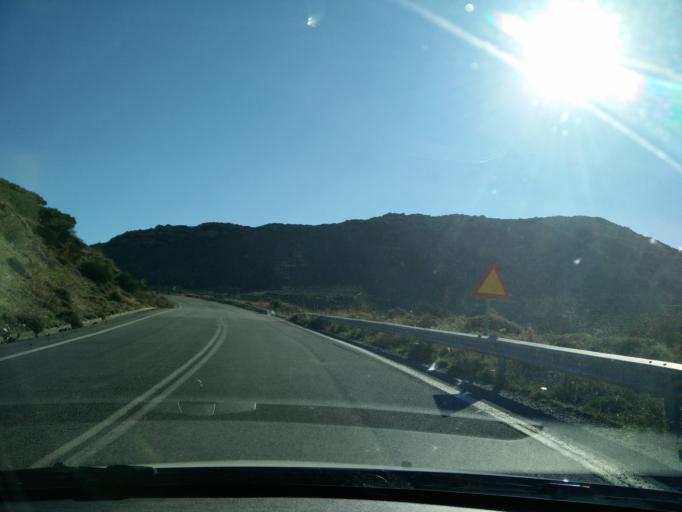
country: GR
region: Crete
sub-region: Nomos Irakleiou
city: Arkalochori
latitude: 35.0678
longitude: 25.3544
